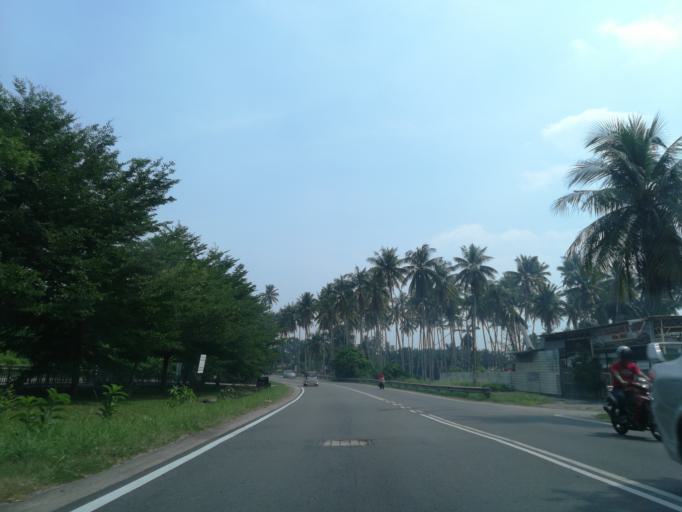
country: MY
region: Penang
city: Tasek Glugor
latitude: 5.4270
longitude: 100.5365
